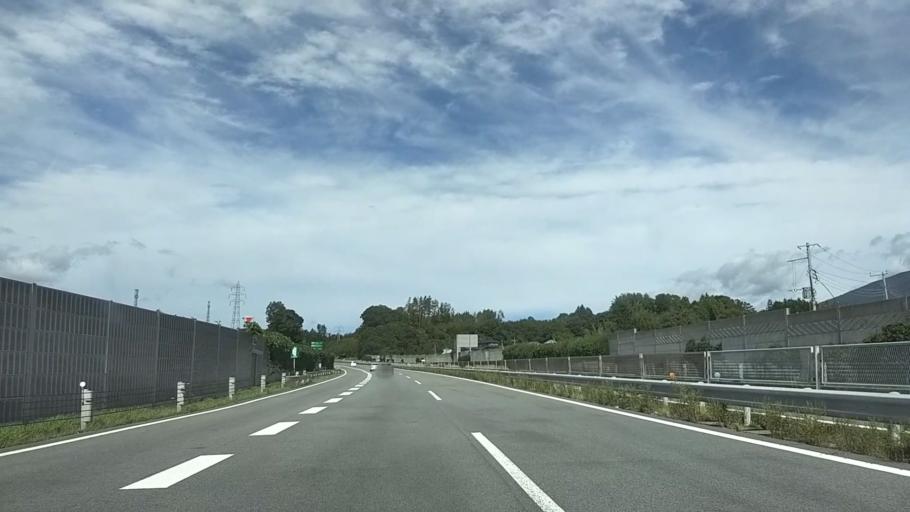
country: JP
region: Yamanashi
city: Nirasaki
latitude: 35.8424
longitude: 138.3807
